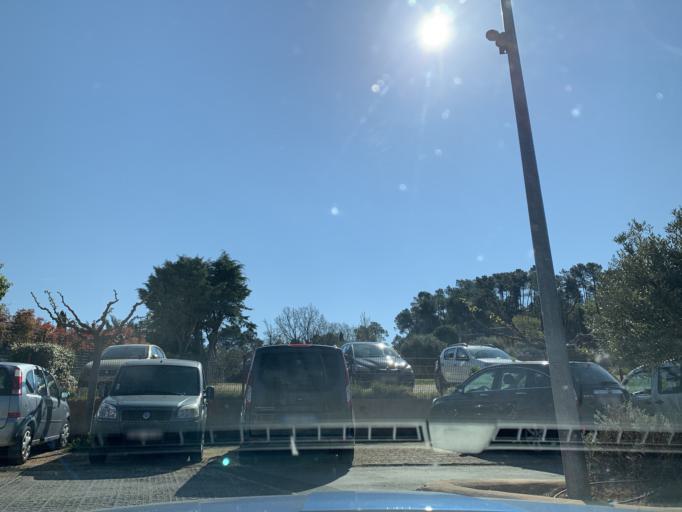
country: FR
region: Provence-Alpes-Cote d'Azur
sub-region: Departement du Vaucluse
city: Roussillon
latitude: 43.9010
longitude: 5.2946
